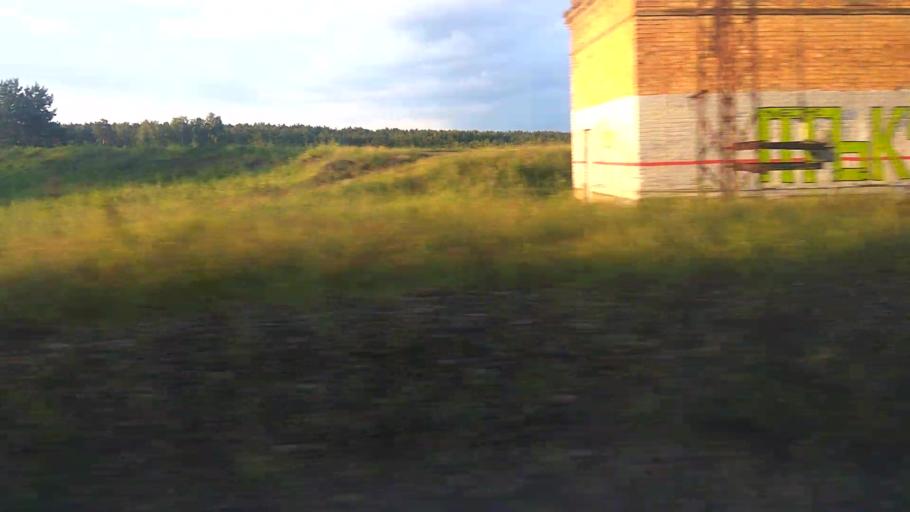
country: RU
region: Moskovskaya
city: Kashira
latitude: 54.8666
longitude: 38.1570
